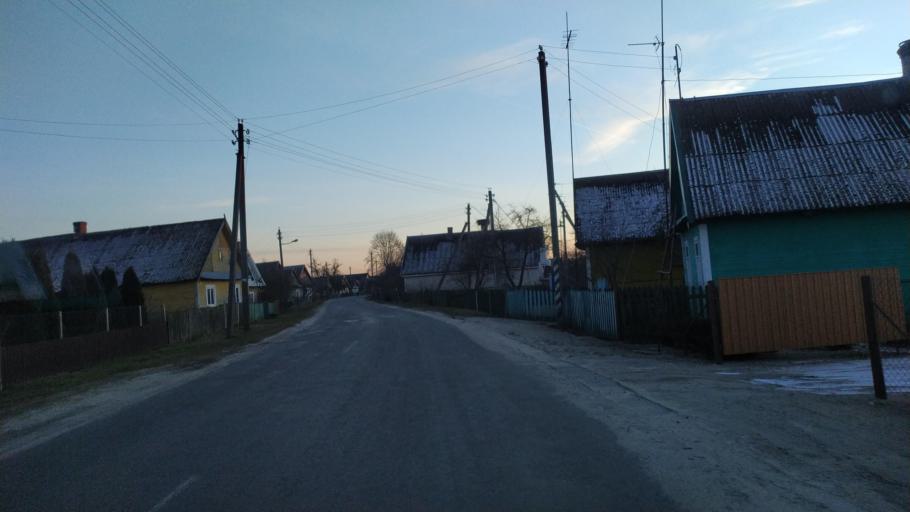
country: BY
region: Brest
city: Pruzhany
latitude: 52.5505
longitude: 24.2107
